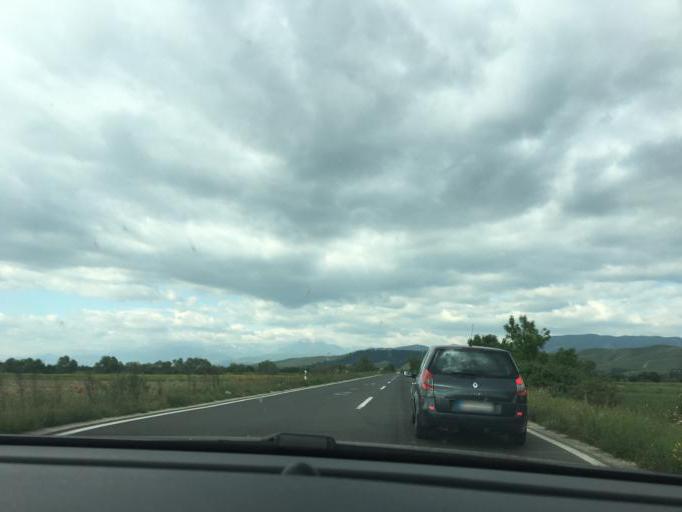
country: MK
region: Prilep
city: Topolcani
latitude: 41.2186
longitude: 21.4303
